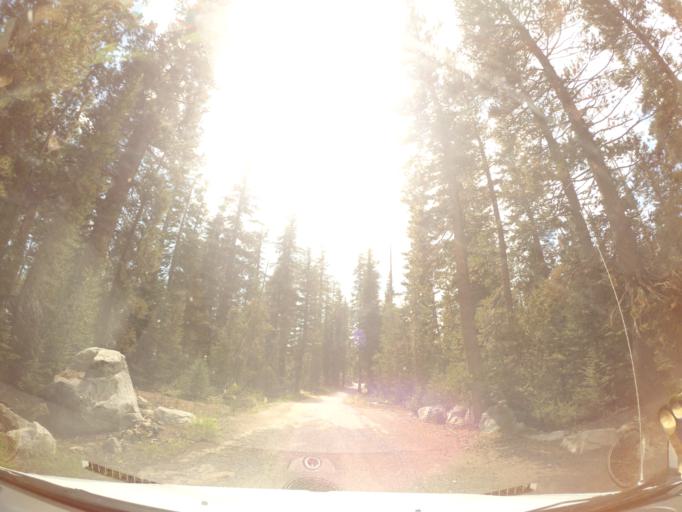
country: US
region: California
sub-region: Mariposa County
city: Yosemite Valley
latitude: 37.8186
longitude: -119.5091
